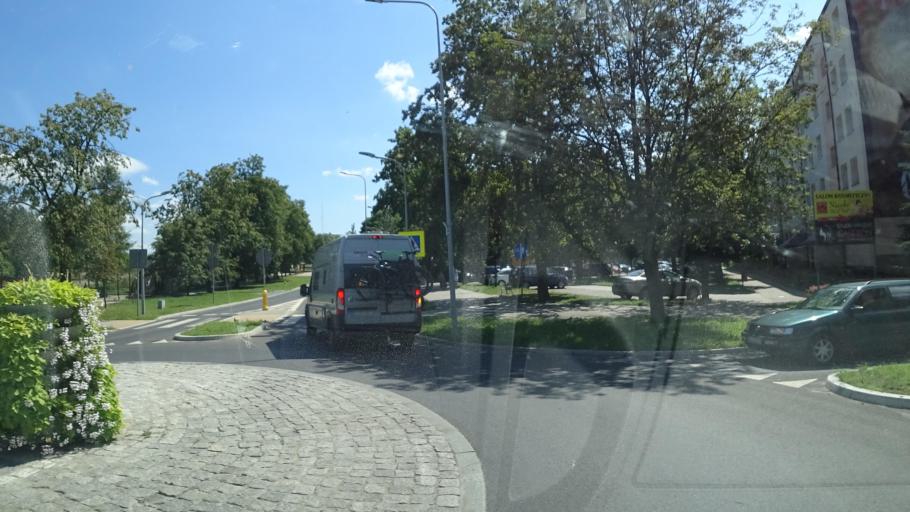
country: PL
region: Podlasie
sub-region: Lomza
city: Lomza
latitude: 53.1764
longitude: 22.0768
